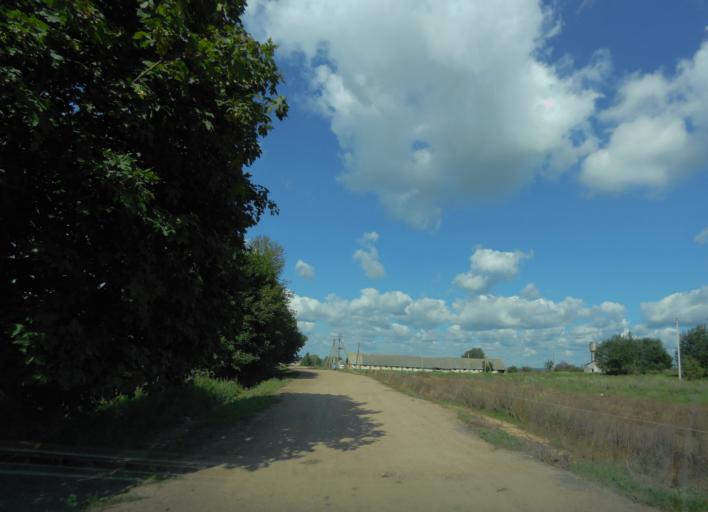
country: BY
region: Minsk
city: Zyembin
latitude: 54.4101
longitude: 28.3850
